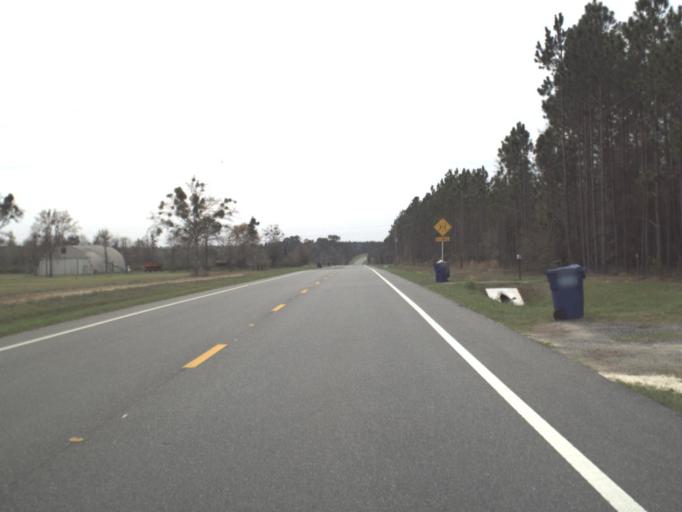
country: US
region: Florida
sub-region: Calhoun County
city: Blountstown
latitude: 30.3668
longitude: -85.2139
